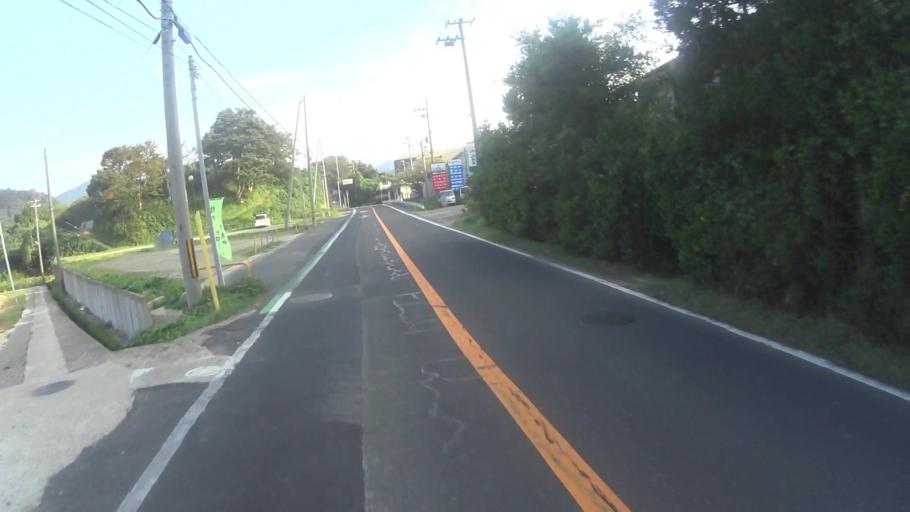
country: JP
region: Kyoto
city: Miyazu
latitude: 35.7228
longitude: 135.1014
